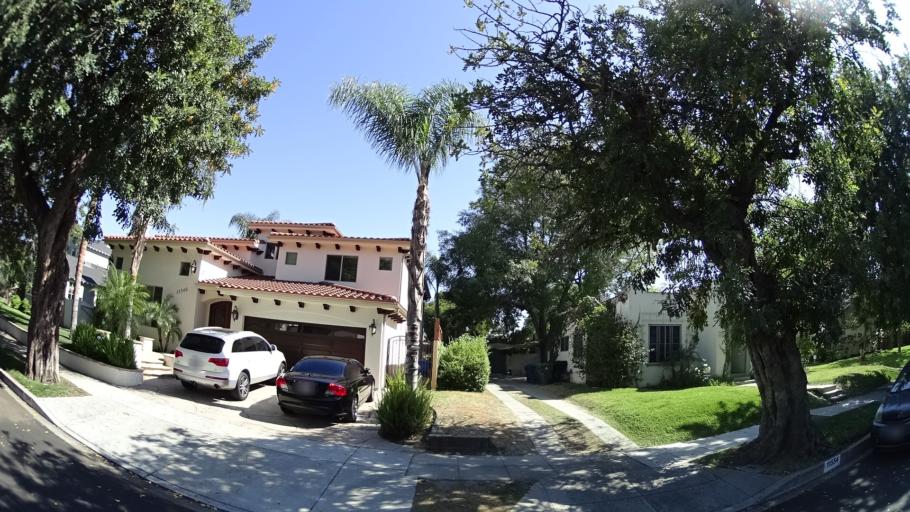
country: US
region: California
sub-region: Los Angeles County
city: North Hollywood
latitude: 34.1595
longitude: -118.3840
